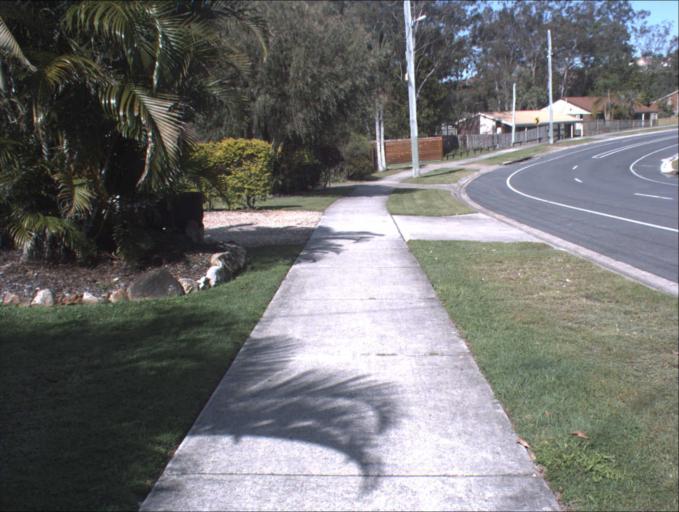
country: AU
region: Queensland
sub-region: Logan
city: Waterford West
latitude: -27.6975
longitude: 153.1604
